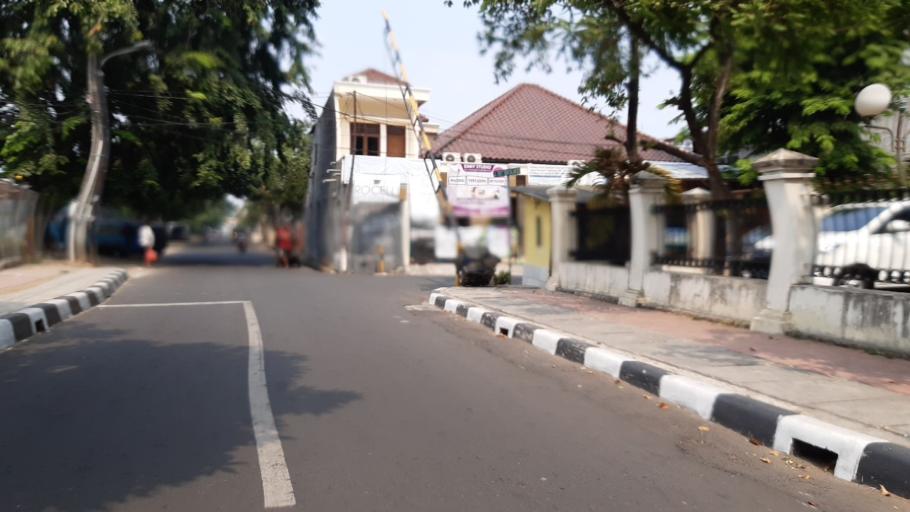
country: ID
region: Jakarta Raya
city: Jakarta
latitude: -6.2290
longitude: 106.8583
